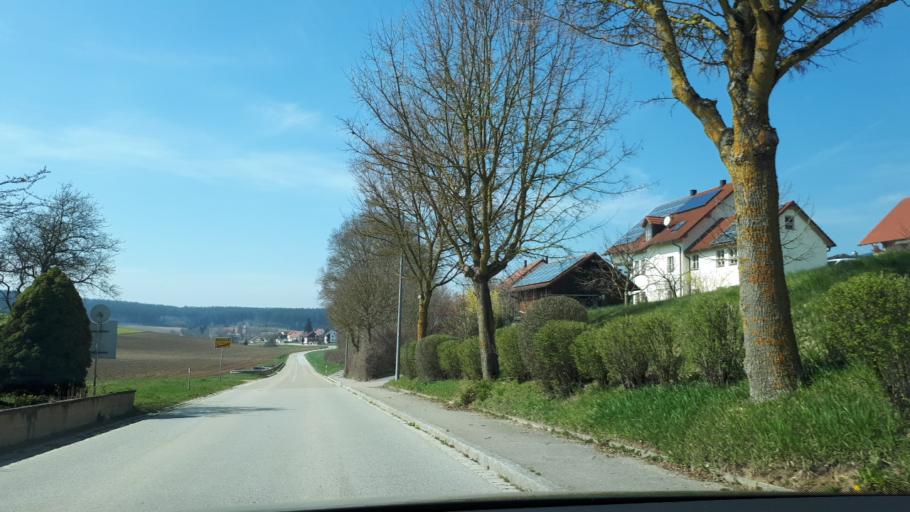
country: DE
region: Bavaria
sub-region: Lower Bavaria
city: Kelheim
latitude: 48.8803
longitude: 11.8866
